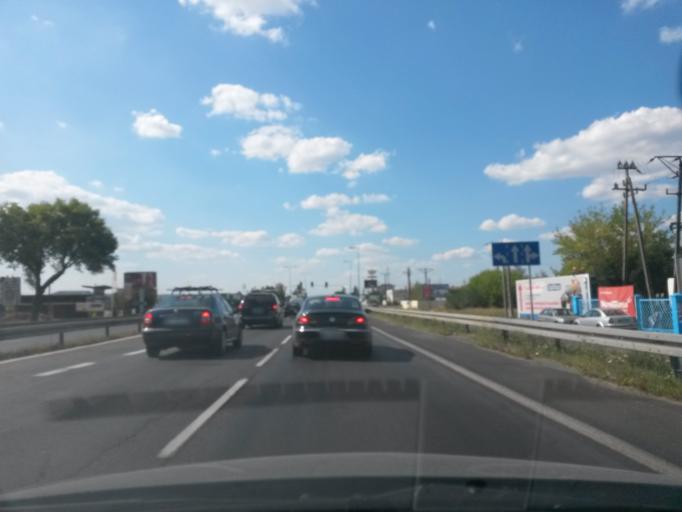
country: PL
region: Masovian Voivodeship
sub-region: Powiat warszawski zachodni
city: Dziekanow Lesny
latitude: 52.3575
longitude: 20.8356
